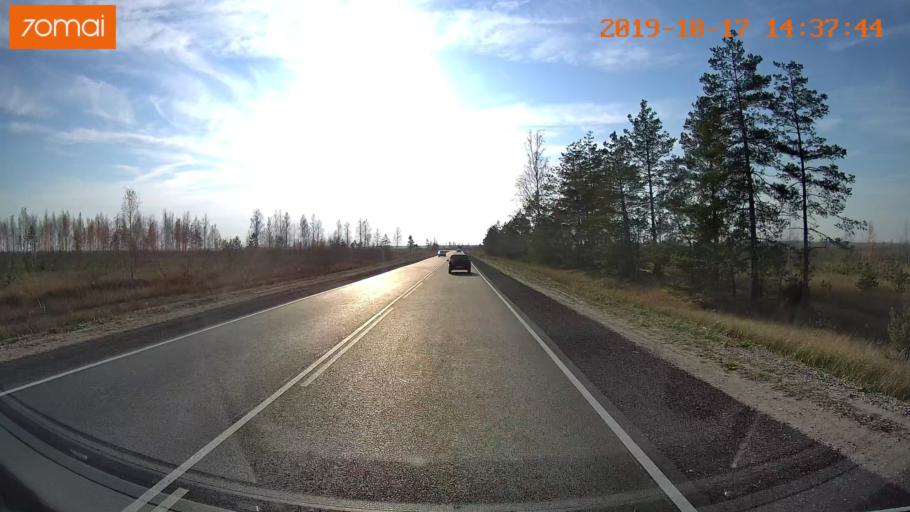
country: RU
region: Rjazan
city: Solotcha
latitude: 54.8774
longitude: 39.9921
